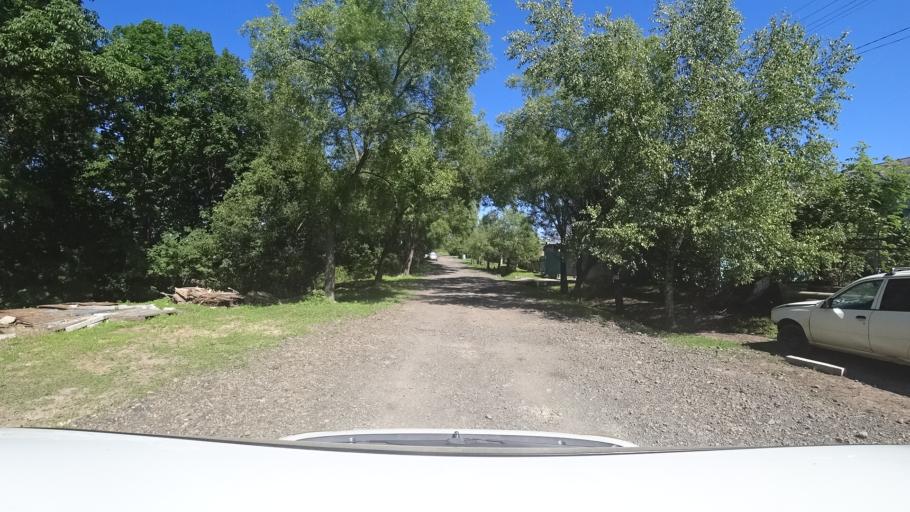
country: RU
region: Khabarovsk Krai
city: Topolevo
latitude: 48.5607
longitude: 135.1938
